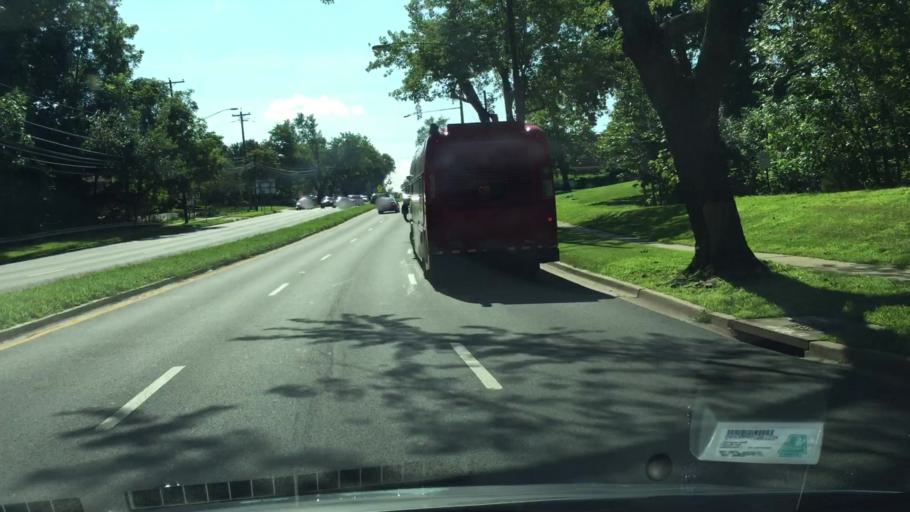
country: US
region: Maryland
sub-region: Montgomery County
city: Glenmont
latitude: 39.0591
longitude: -77.0635
